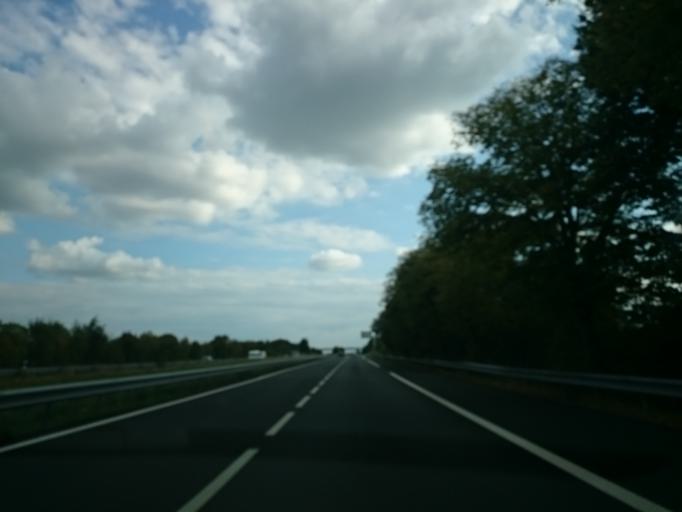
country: FR
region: Pays de la Loire
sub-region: Departement de la Loire-Atlantique
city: La Grigonnais
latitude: 47.4946
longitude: -1.6382
